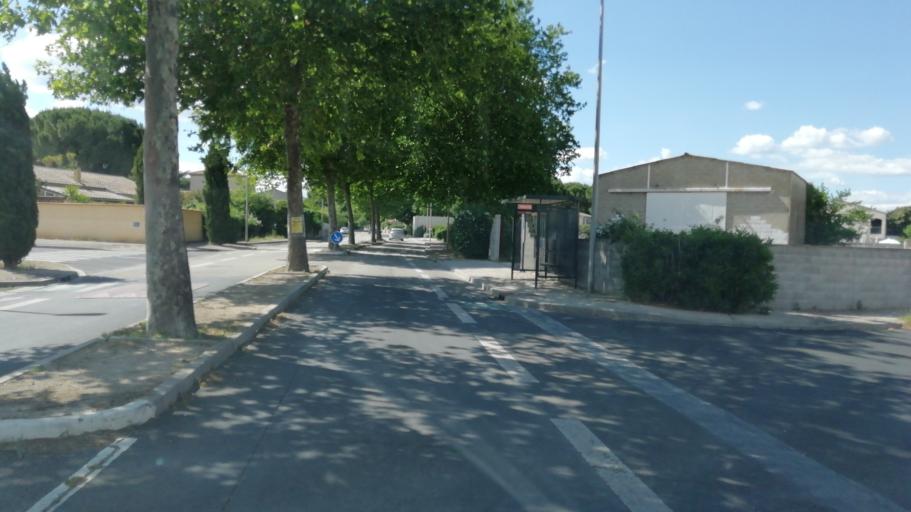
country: FR
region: Languedoc-Roussillon
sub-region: Departement de l'Herault
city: Lunel-Viel
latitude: 43.6746
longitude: 4.0972
